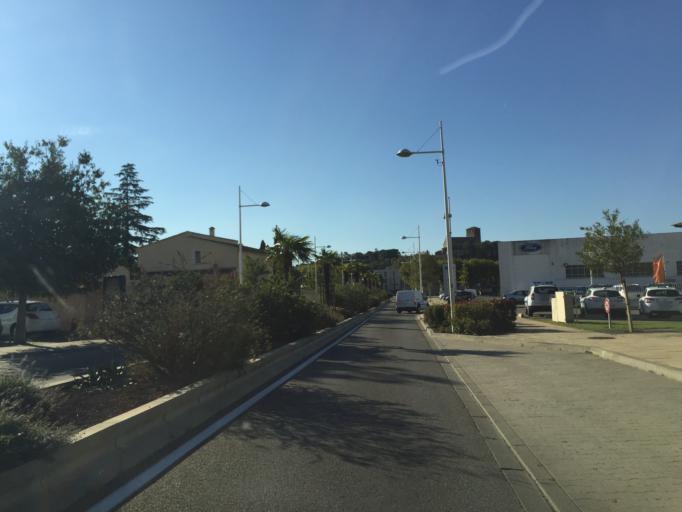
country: FR
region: Provence-Alpes-Cote d'Azur
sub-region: Departement du Vaucluse
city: Bollene
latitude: 44.2839
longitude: 4.7508
